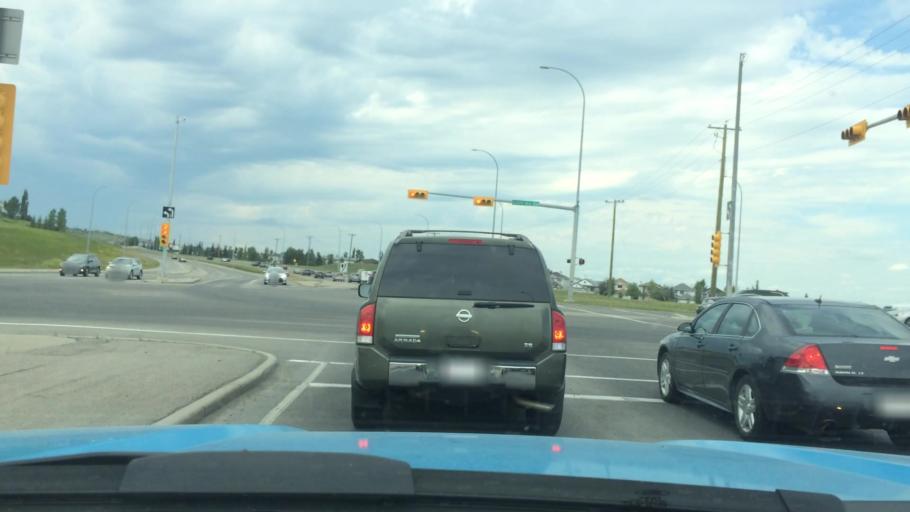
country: CA
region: Alberta
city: Calgary
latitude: 51.1424
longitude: -114.1232
